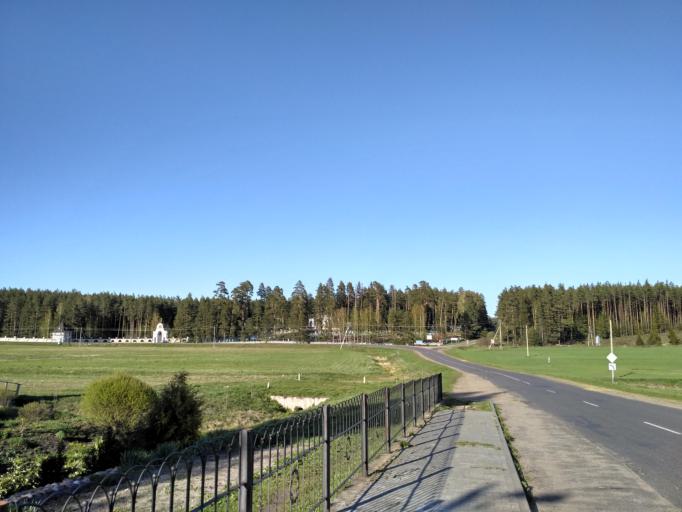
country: BY
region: Minsk
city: Loshnitsa
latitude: 54.4923
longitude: 28.6760
